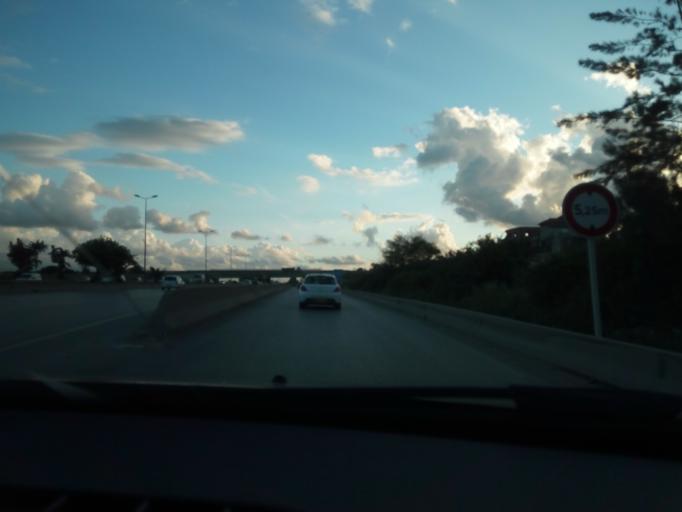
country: DZ
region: Tipaza
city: Saoula
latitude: 36.6528
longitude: 3.0162
